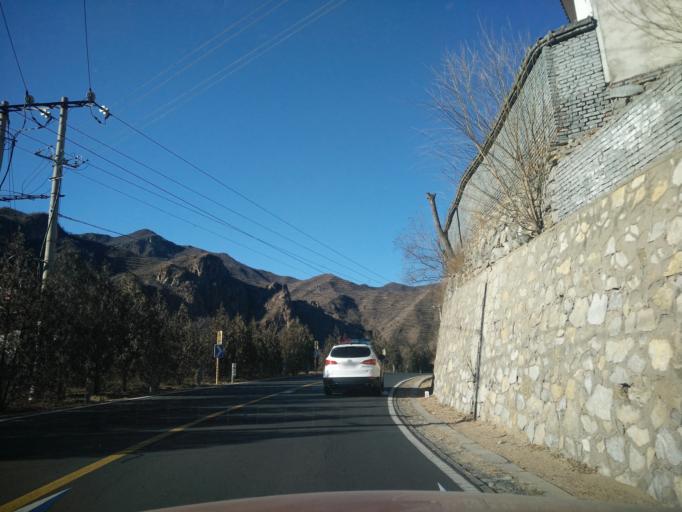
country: CN
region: Beijing
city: Yanchi
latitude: 40.0195
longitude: 115.8670
